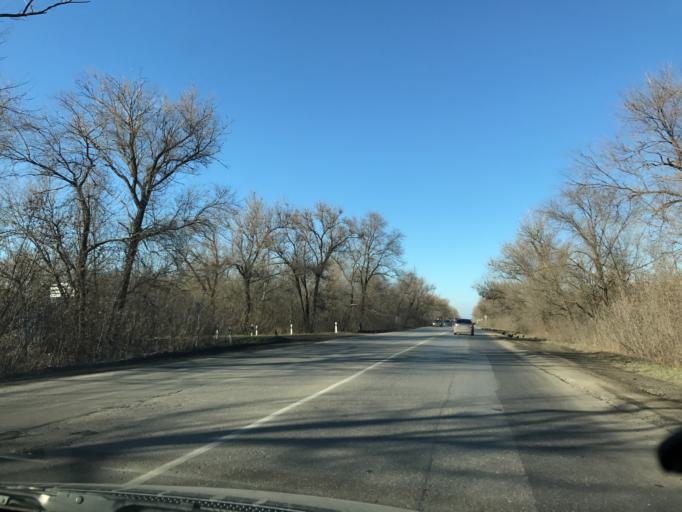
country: RU
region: Rostov
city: Bataysk
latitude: 47.0457
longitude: 39.8476
